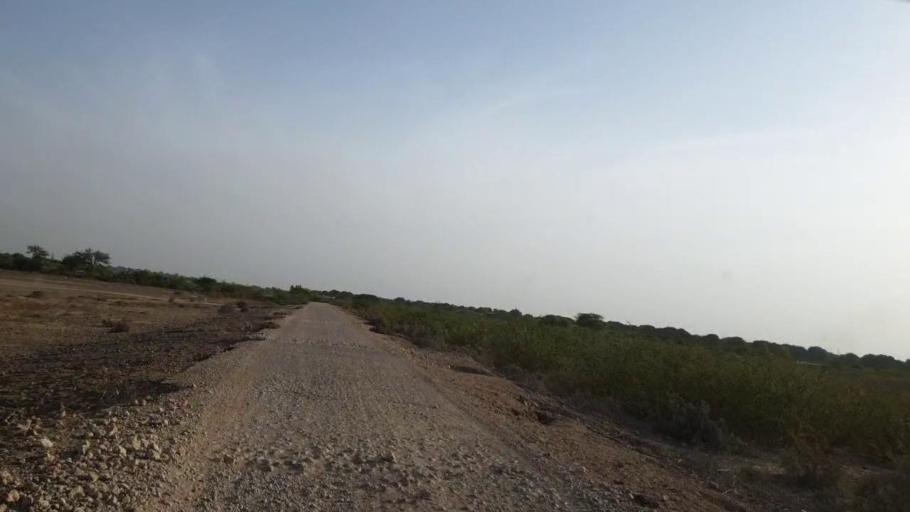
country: PK
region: Sindh
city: Kunri
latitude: 25.0752
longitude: 69.4438
